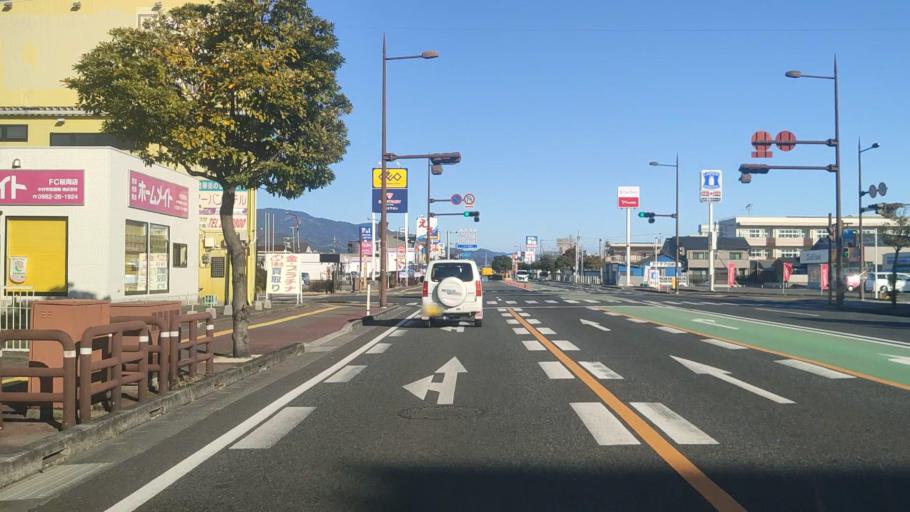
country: JP
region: Miyazaki
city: Nobeoka
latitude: 32.5715
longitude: 131.6836
